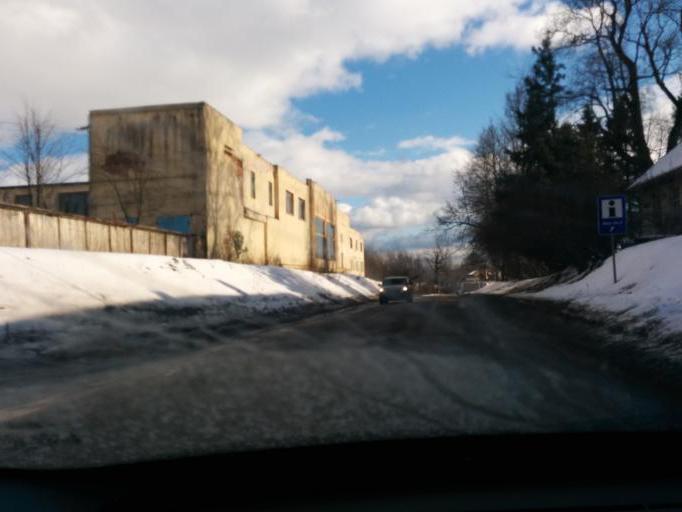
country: LV
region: Gulbenes Rajons
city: Gulbene
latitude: 57.1848
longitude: 26.7346
